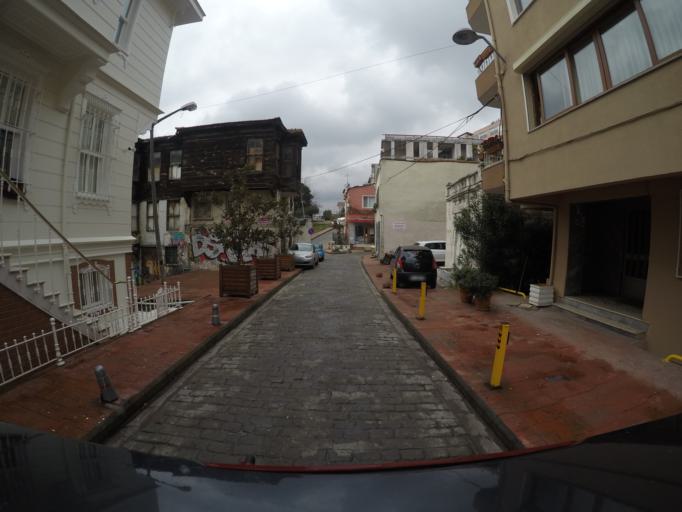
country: TR
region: Istanbul
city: Eminoenue
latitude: 41.0292
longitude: 28.9847
